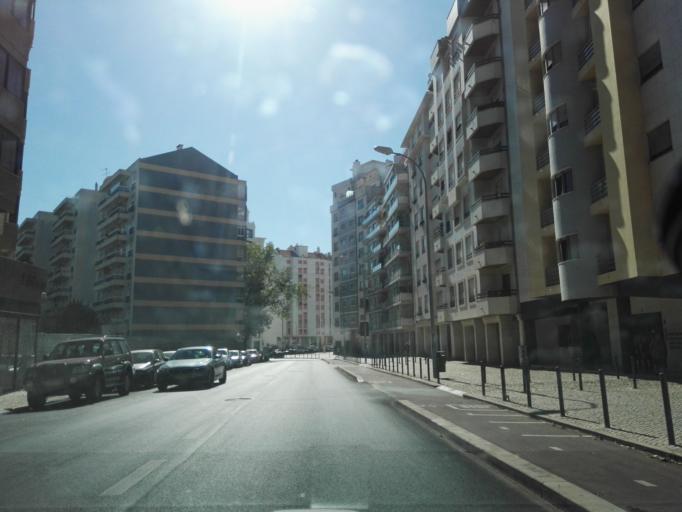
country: PT
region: Lisbon
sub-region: Odivelas
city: Pontinha
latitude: 38.7514
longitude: -9.1903
